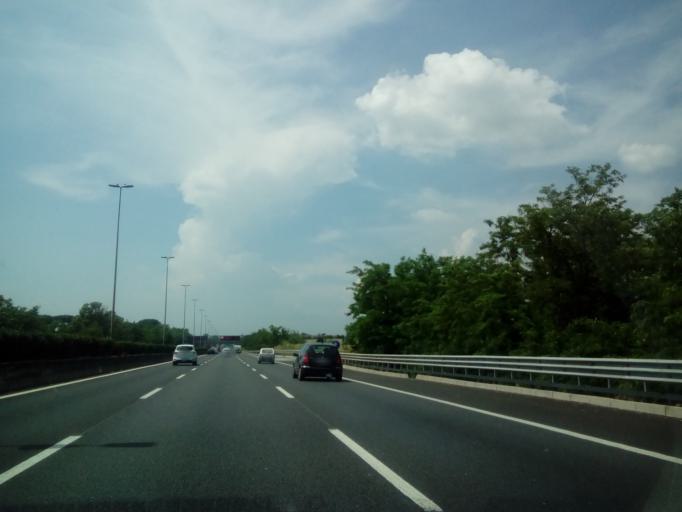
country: IT
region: Latium
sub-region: Citta metropolitana di Roma Capitale
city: Colle Verde
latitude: 41.9635
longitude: 12.5695
